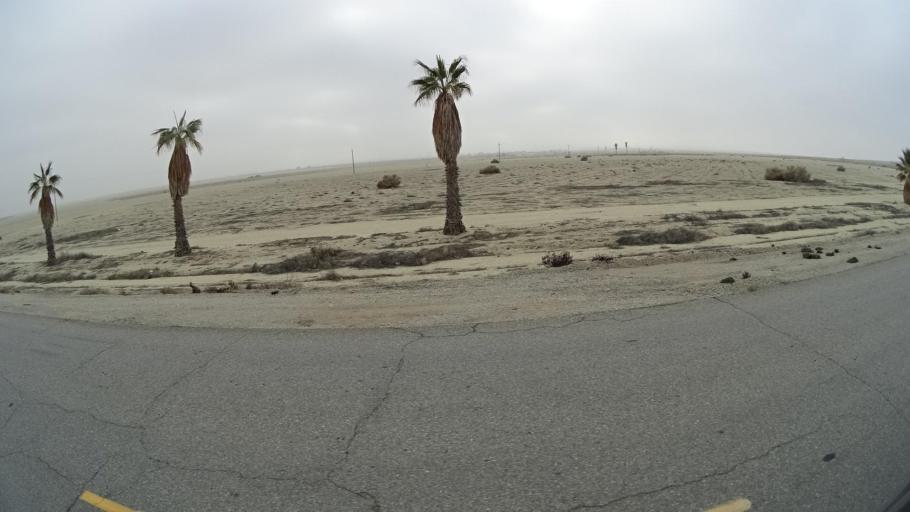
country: US
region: California
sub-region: Kern County
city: Maricopa
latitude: 35.1242
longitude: -119.3623
